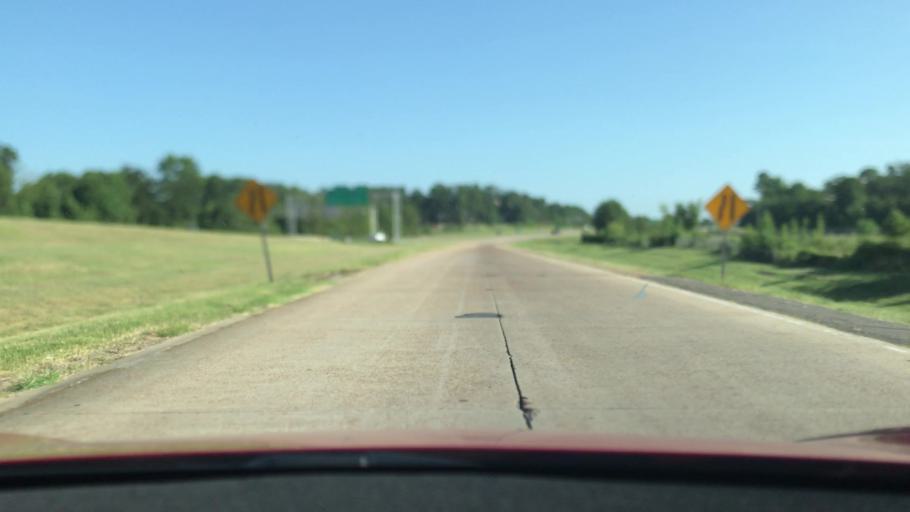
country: US
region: Louisiana
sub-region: Caddo Parish
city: Shreveport
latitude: 32.4433
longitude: -93.8415
